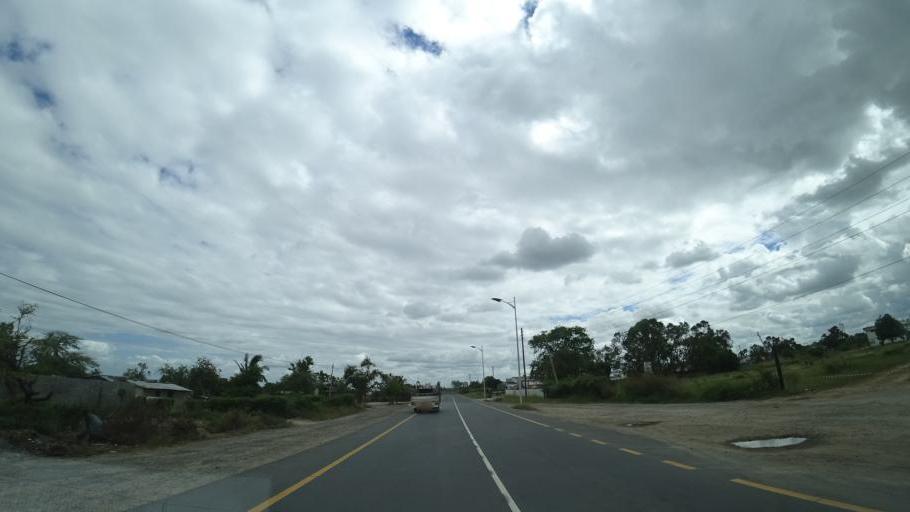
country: MZ
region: Sofala
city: Dondo
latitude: -19.4973
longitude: 34.5932
